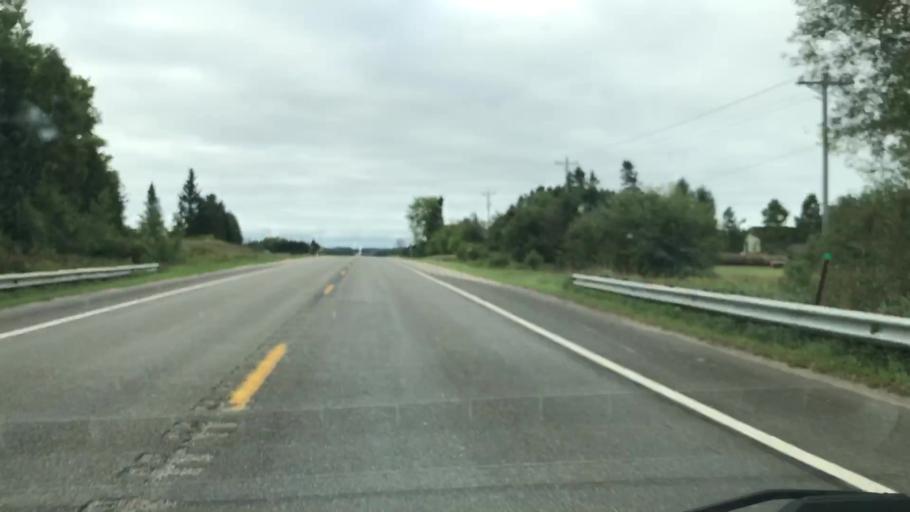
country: US
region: Michigan
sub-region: Luce County
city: Newberry
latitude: 46.1550
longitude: -85.5713
